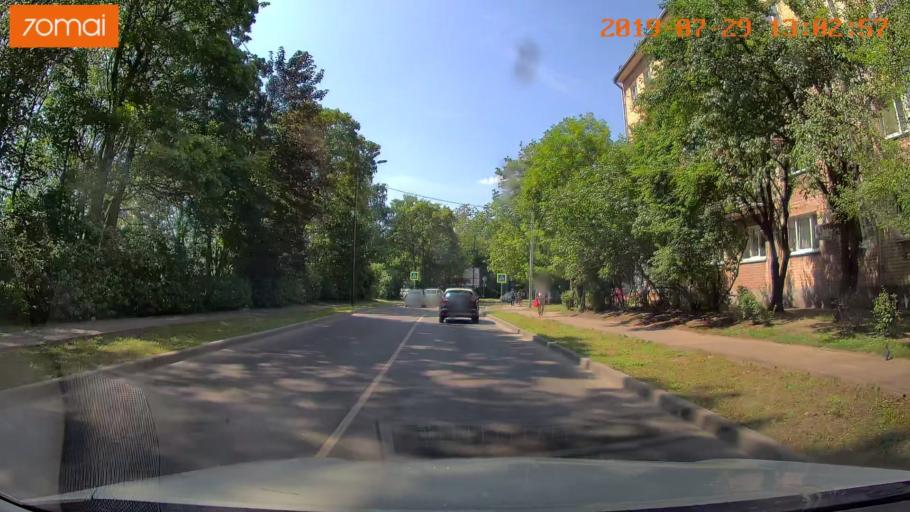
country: RU
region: Kaliningrad
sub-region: Gorod Kaliningrad
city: Kaliningrad
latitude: 54.7153
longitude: 20.4725
